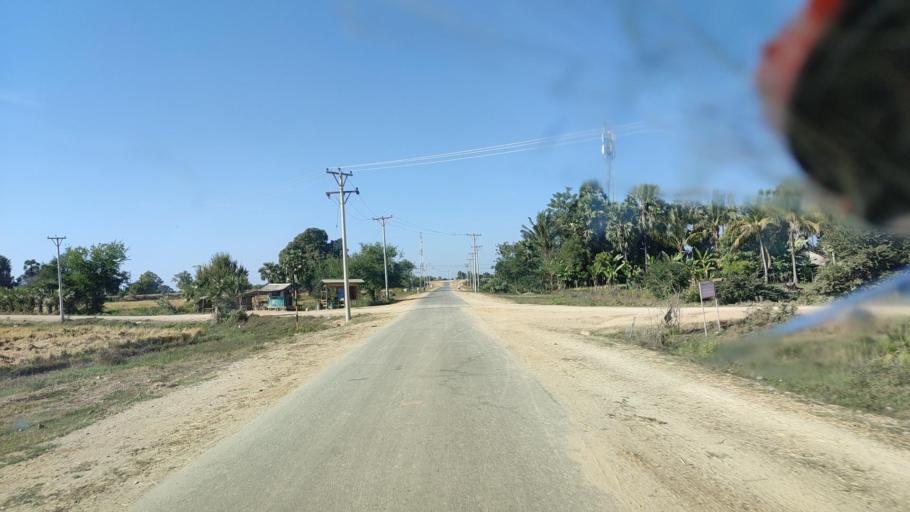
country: MM
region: Mandalay
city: Yamethin
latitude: 20.1480
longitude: 96.2629
